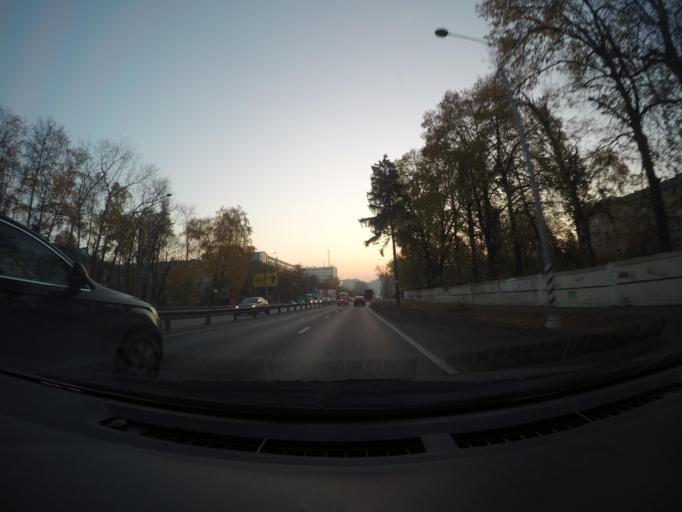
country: RU
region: Moskovskaya
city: Tomilino
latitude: 55.6623
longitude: 37.9601
